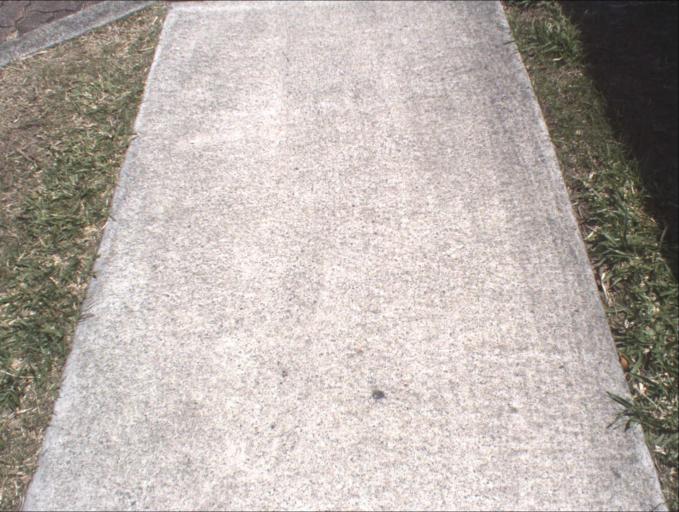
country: AU
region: Queensland
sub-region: Logan
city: Rochedale South
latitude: -27.5970
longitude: 153.1306
